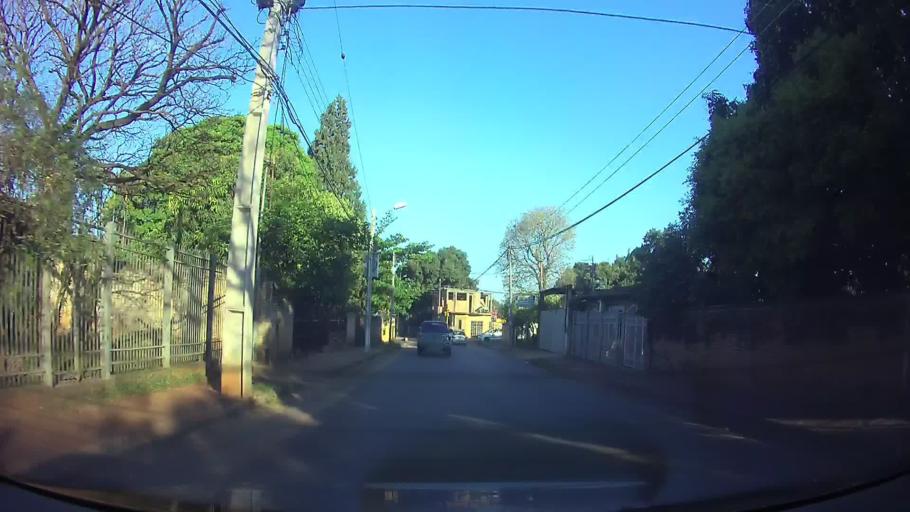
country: PY
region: Central
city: Fernando de la Mora
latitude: -25.3427
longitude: -57.5350
